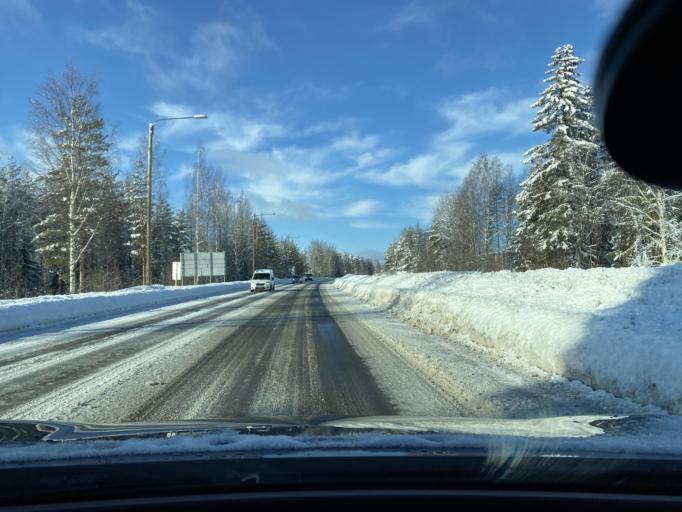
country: FI
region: Southern Savonia
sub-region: Mikkeli
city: Kangasniemi
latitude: 62.0035
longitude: 26.6544
